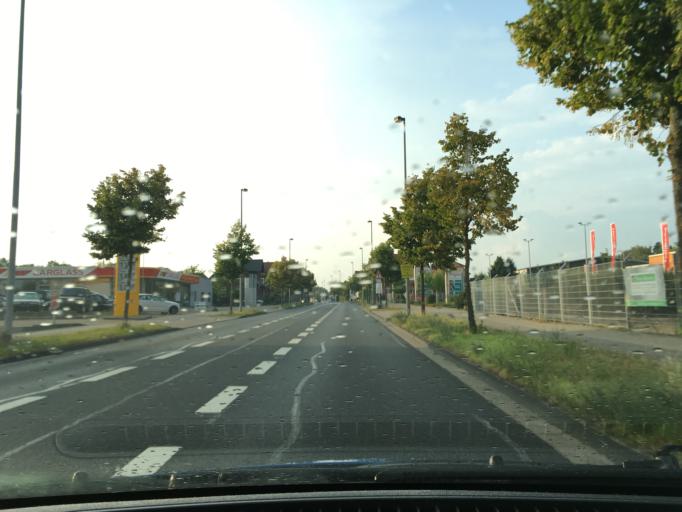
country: DE
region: Lower Saxony
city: Celle
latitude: 52.6360
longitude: 10.0800
